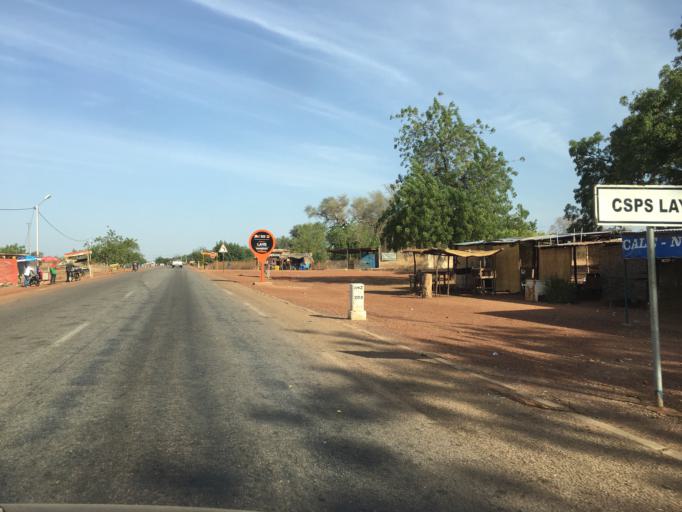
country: BF
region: Plateau-Central
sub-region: Province du Kourweogo
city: Bousse
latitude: 12.5282
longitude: -1.7729
